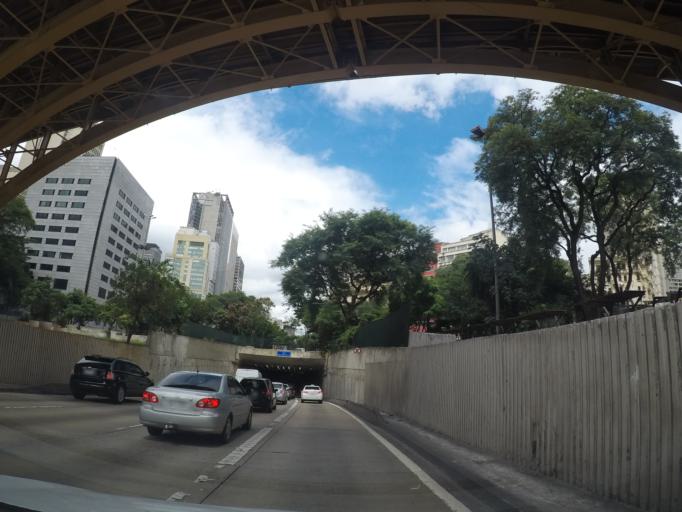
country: BR
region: Sao Paulo
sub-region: Sao Paulo
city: Sao Paulo
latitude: -23.5429
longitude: -46.6337
